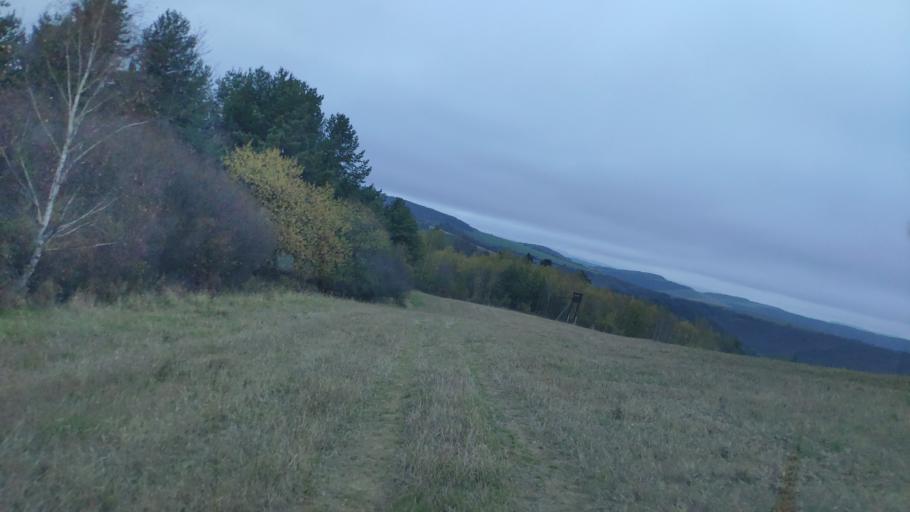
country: SK
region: Presovsky
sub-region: Okres Presov
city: Presov
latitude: 48.9334
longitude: 21.0860
